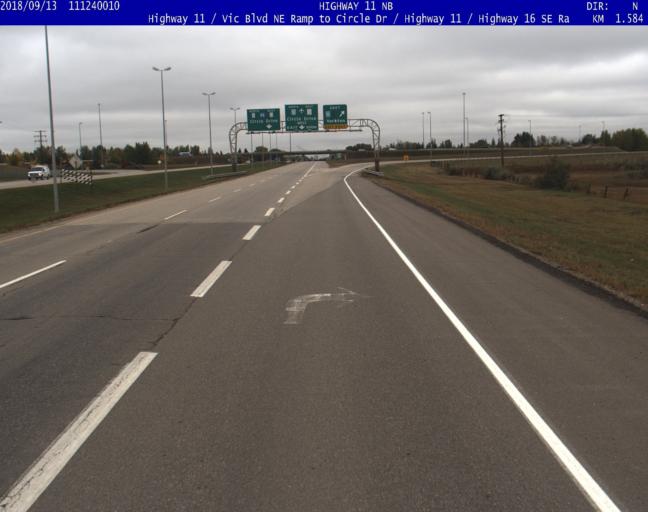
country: CA
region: Saskatchewan
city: Saskatoon
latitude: 52.0840
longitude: -106.6044
